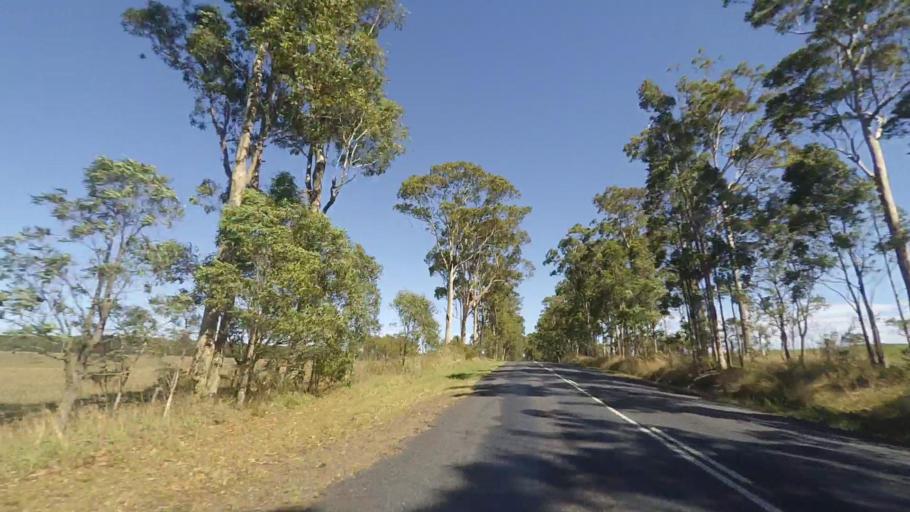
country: AU
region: New South Wales
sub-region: Great Lakes
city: Hawks Nest
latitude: -32.6270
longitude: 152.1319
